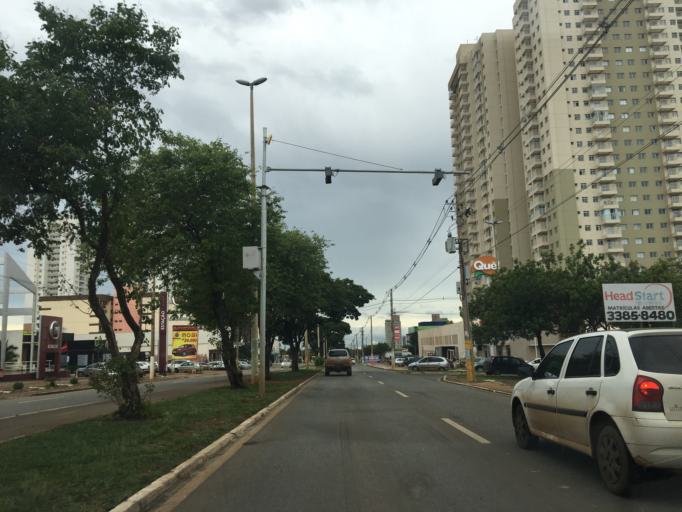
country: BR
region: Goias
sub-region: Luziania
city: Luziania
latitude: -16.0127
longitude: -48.0601
